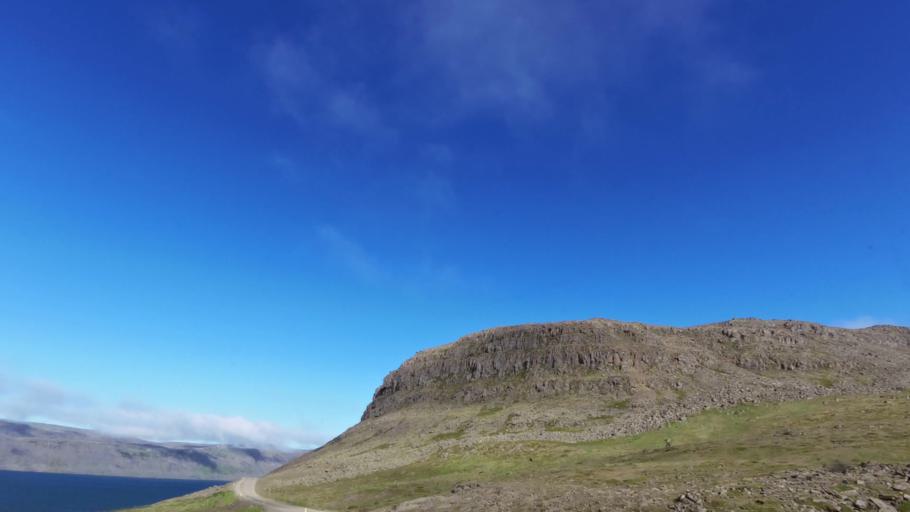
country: IS
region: West
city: Olafsvik
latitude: 65.5613
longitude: -24.0326
